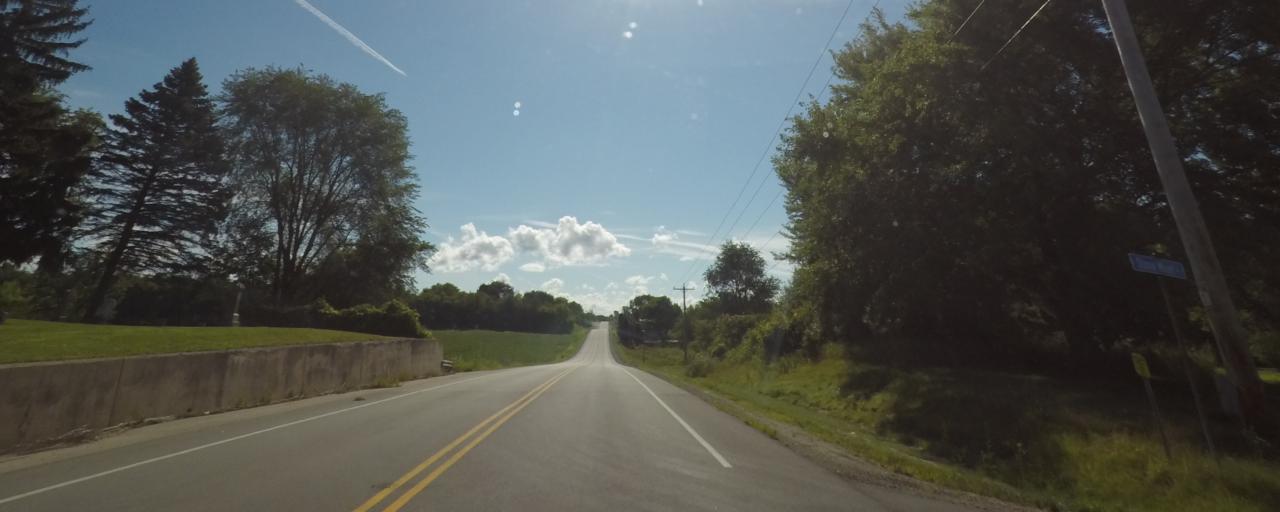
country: US
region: Wisconsin
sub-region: Jefferson County
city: Ixonia
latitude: 43.0735
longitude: -88.6575
